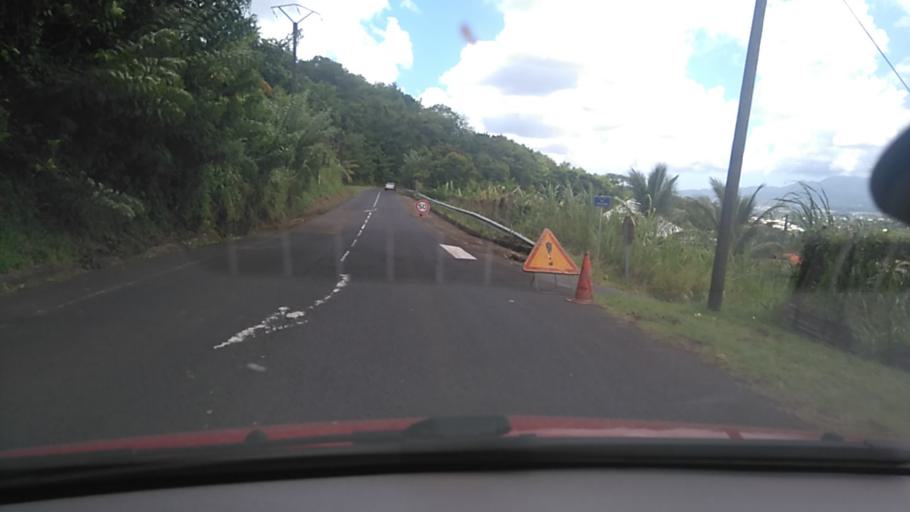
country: MQ
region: Martinique
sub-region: Martinique
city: Saint-Esprit
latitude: 14.5677
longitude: -60.9487
